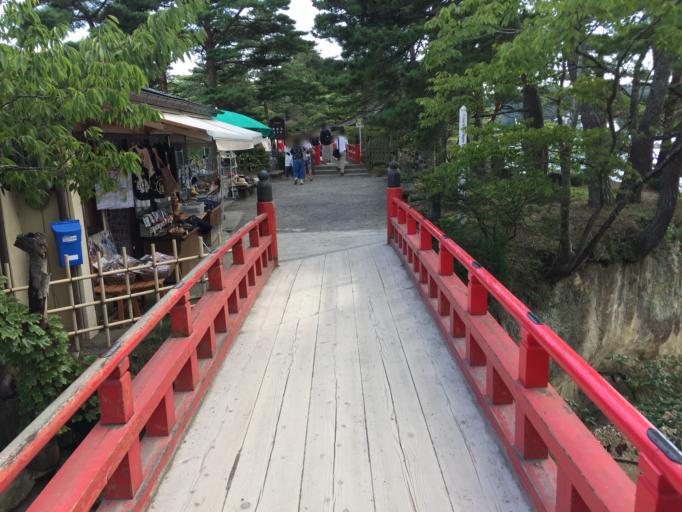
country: JP
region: Miyagi
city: Matsushima
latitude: 38.3703
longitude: 141.0643
